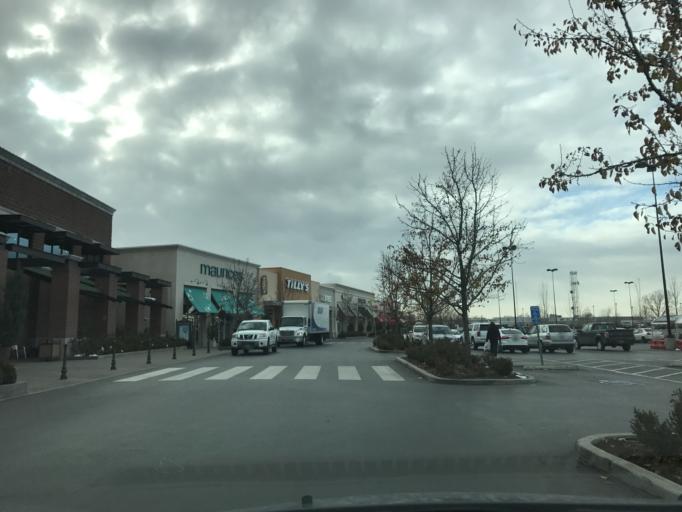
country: US
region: Utah
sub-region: Davis County
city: Farmington
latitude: 40.9841
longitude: -111.9037
